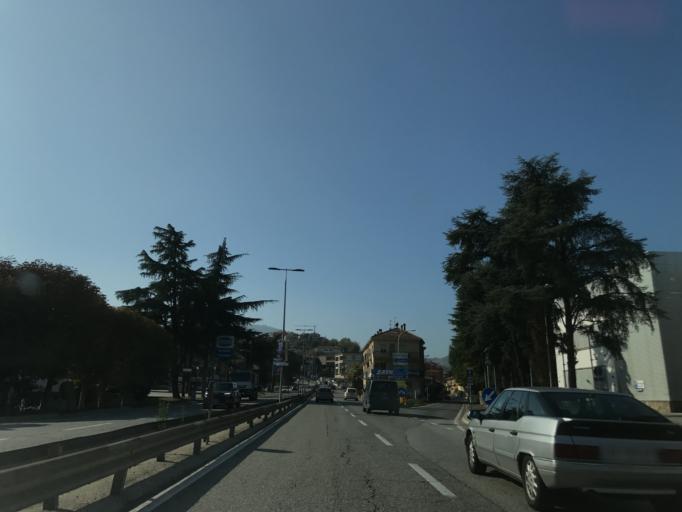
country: SM
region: Serravalle
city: Serravalle
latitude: 43.9743
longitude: 12.4853
